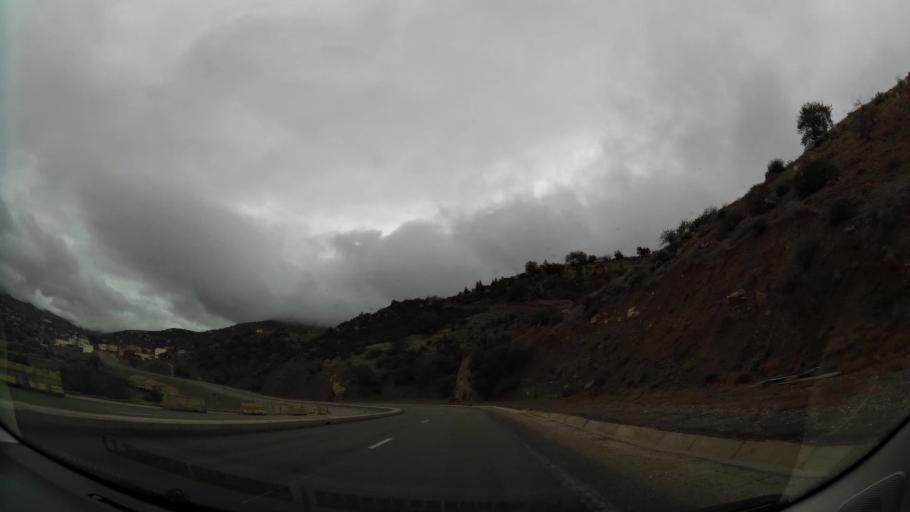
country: MA
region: Taza-Al Hoceima-Taounate
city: Imzourene
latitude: 34.9741
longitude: -3.8135
